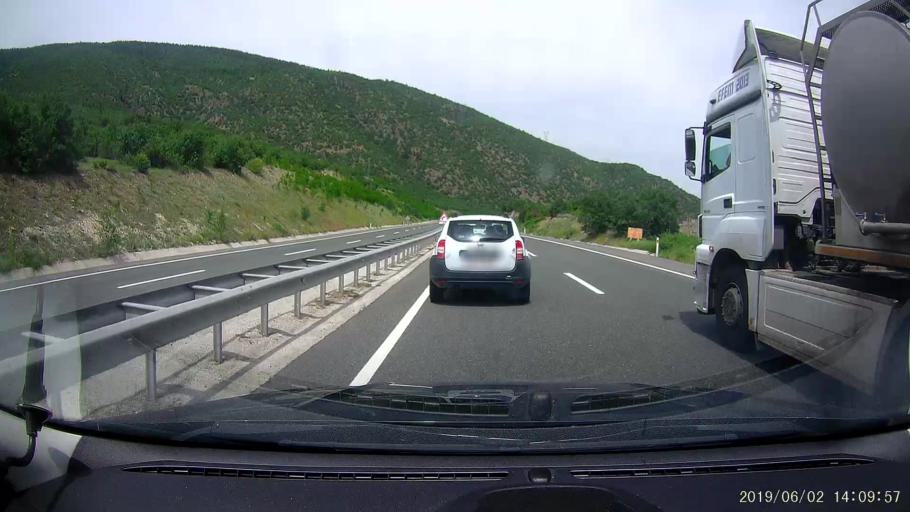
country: TR
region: Cankiri
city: Ilgaz
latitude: 40.8992
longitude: 33.7506
